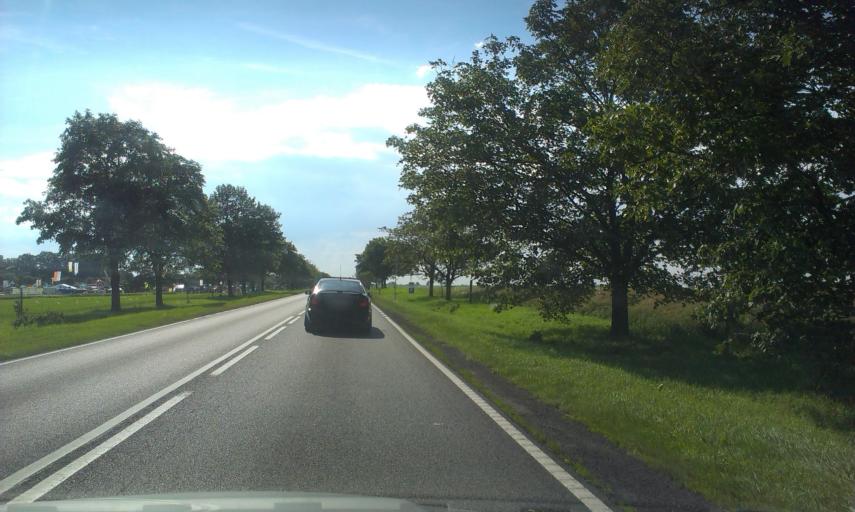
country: PL
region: Kujawsko-Pomorskie
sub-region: Powiat nakielski
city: Slesin
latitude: 53.1675
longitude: 17.7513
